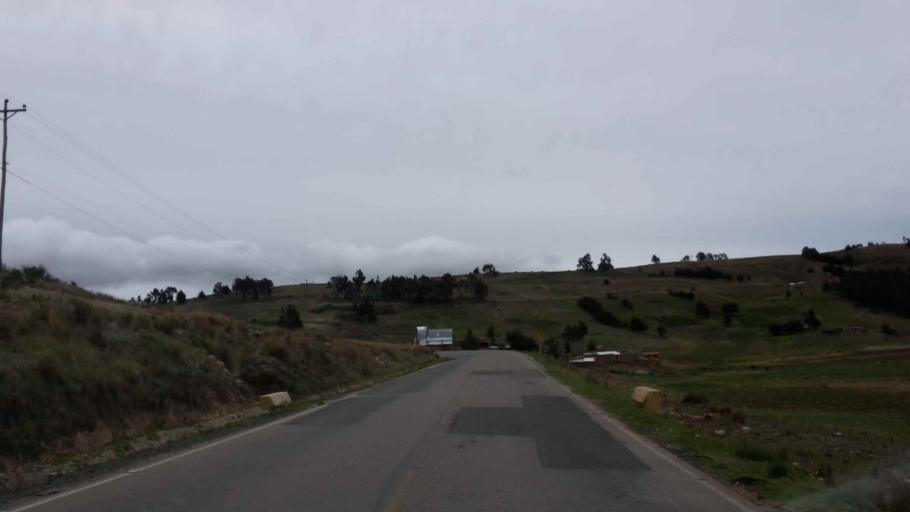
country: BO
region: Cochabamba
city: Arani
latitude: -17.4789
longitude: -65.5977
